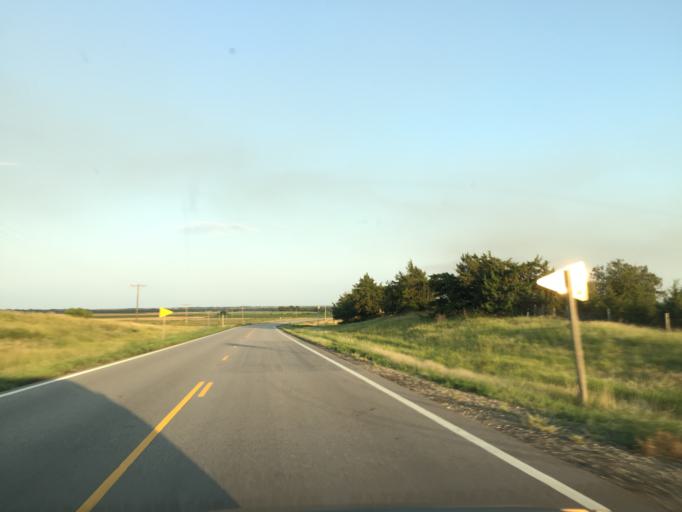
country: US
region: Kansas
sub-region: Ellsworth County
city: Ellsworth
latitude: 38.6953
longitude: -98.2077
